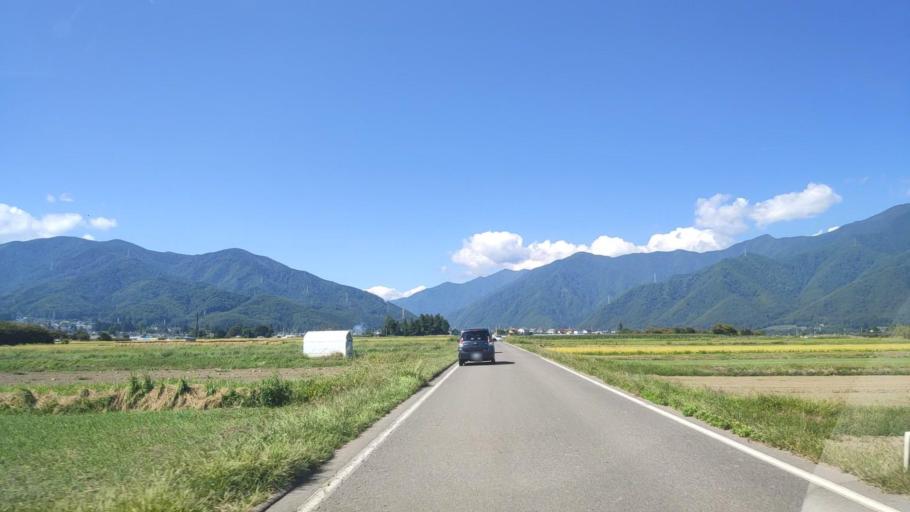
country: JP
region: Nagano
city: Matsumoto
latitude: 36.1979
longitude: 137.8733
